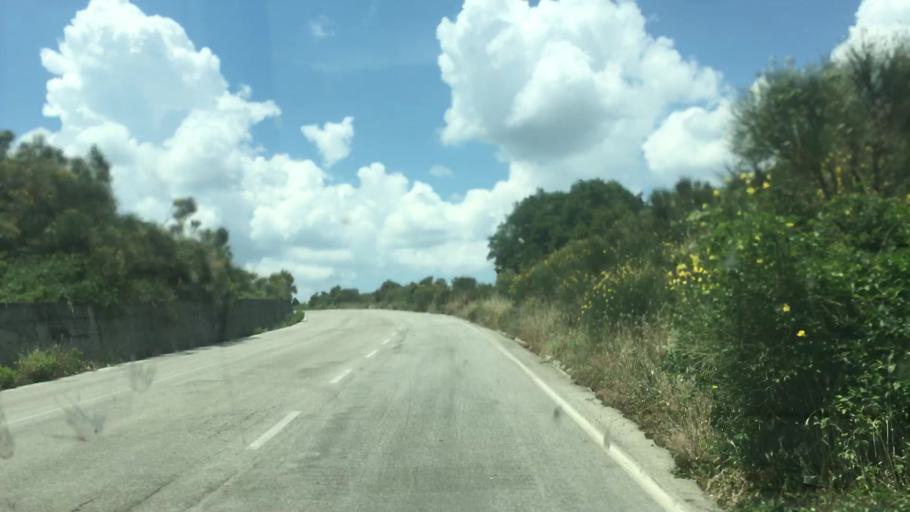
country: IT
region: Basilicate
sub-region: Provincia di Potenza
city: Tolve
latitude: 40.6862
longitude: 15.9821
